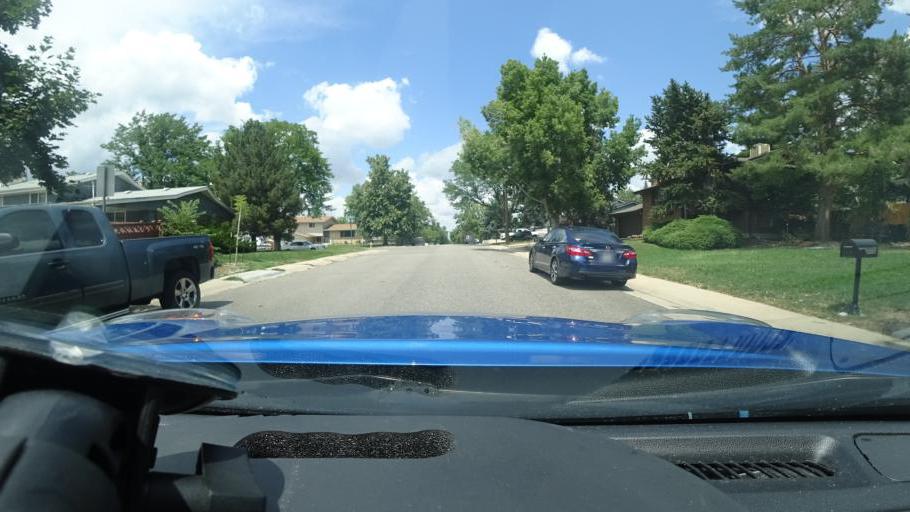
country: US
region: Colorado
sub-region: Adams County
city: Aurora
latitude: 39.7028
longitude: -104.8350
